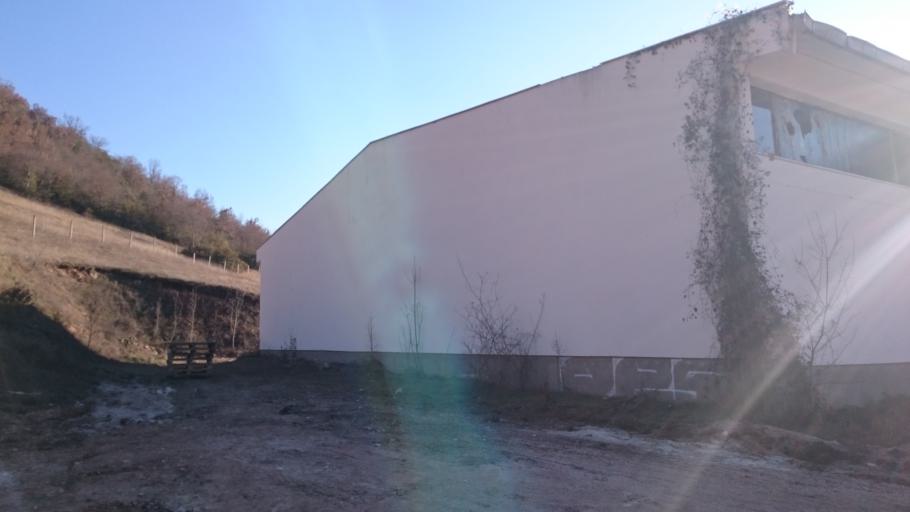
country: MK
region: Makedonski Brod
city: Makedonski Brod
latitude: 41.5462
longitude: 21.2503
